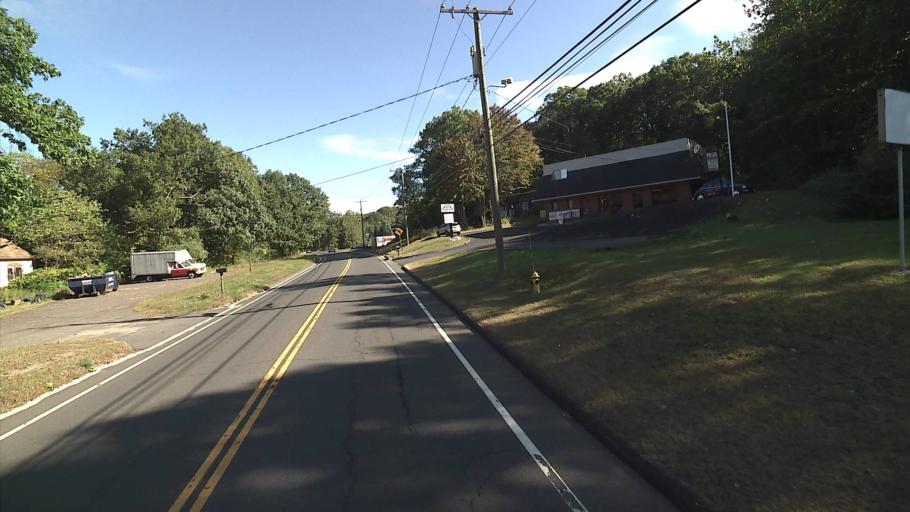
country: US
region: Connecticut
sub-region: New Haven County
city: Wolcott
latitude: 41.5963
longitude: -72.9862
